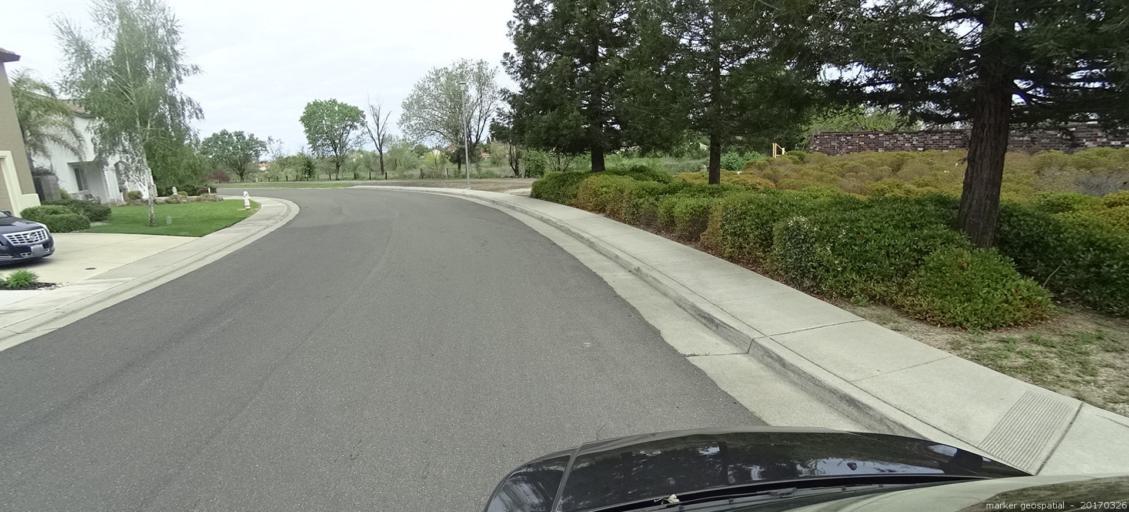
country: US
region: California
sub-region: Sacramento County
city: Laguna
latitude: 38.4410
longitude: -121.4381
